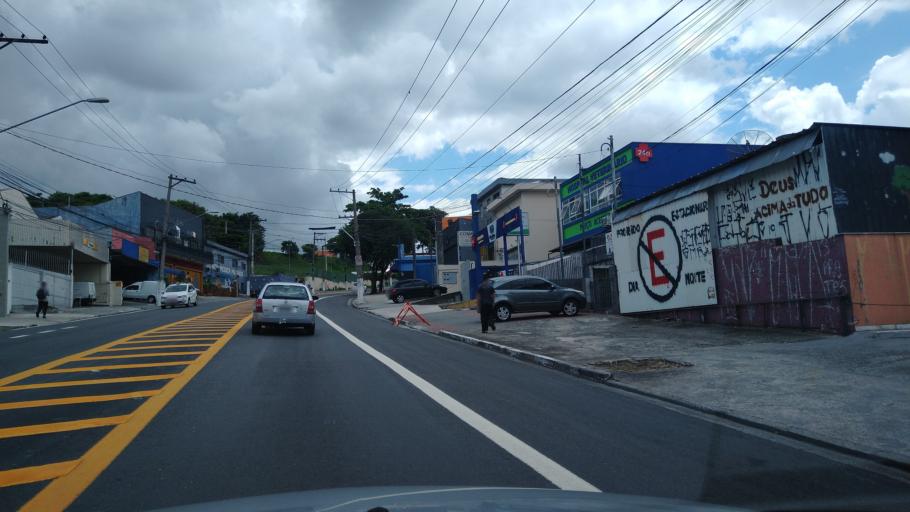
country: BR
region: Sao Paulo
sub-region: Osasco
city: Osasco
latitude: -23.4881
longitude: -46.7330
